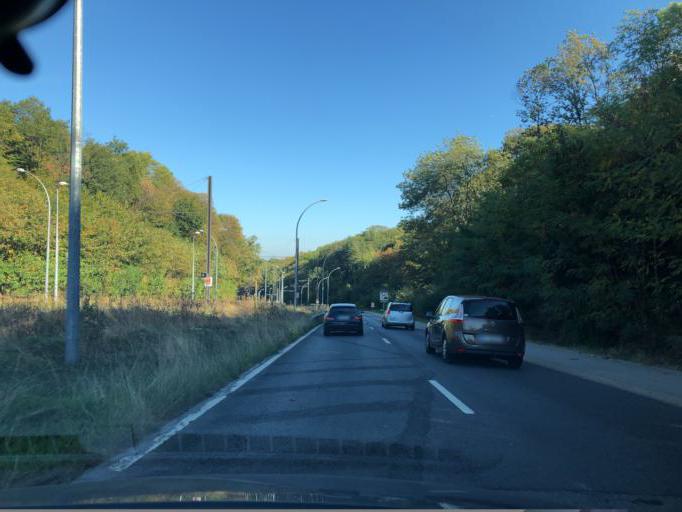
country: FR
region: Ile-de-France
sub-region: Departement des Yvelines
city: Velizy-Villacoublay
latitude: 48.7889
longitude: 2.1798
